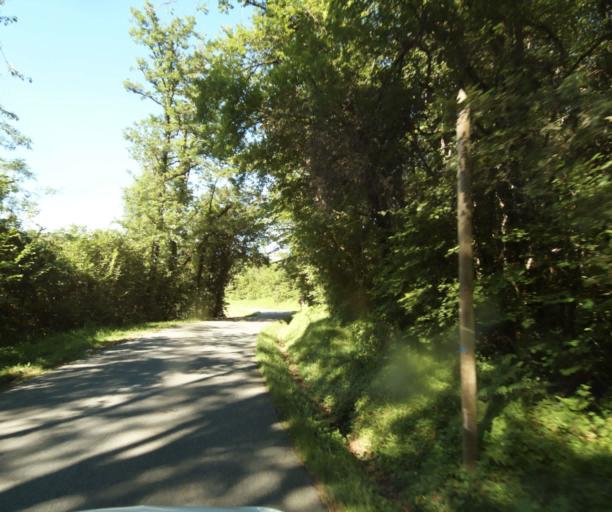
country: FR
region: Rhone-Alpes
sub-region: Departement de la Haute-Savoie
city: Massongy
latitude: 46.3122
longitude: 6.3436
